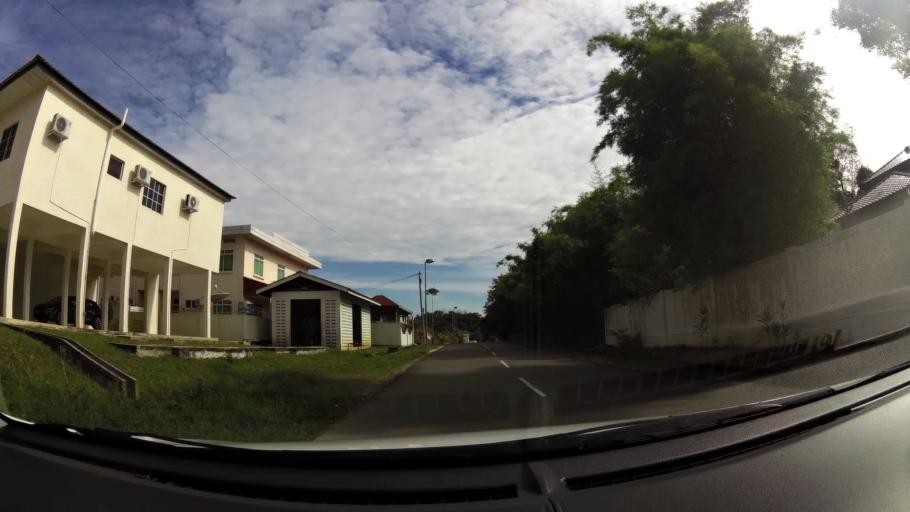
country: BN
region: Brunei and Muara
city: Bandar Seri Begawan
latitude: 4.9238
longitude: 114.9017
